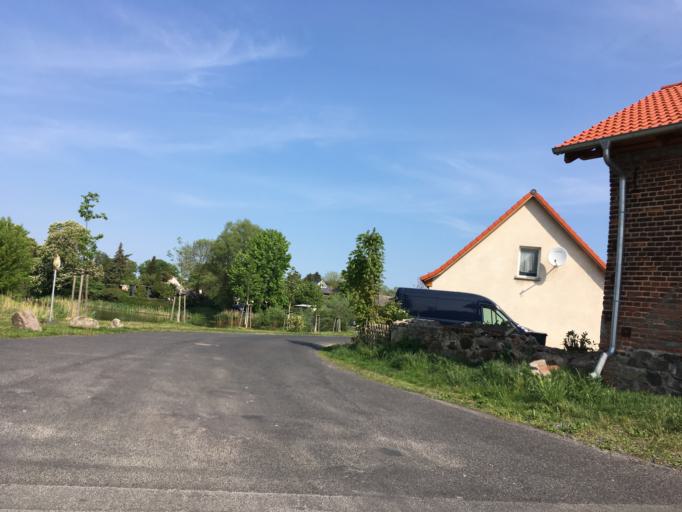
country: DE
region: Berlin
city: Hellersdorf
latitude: 52.5690
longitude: 13.6207
